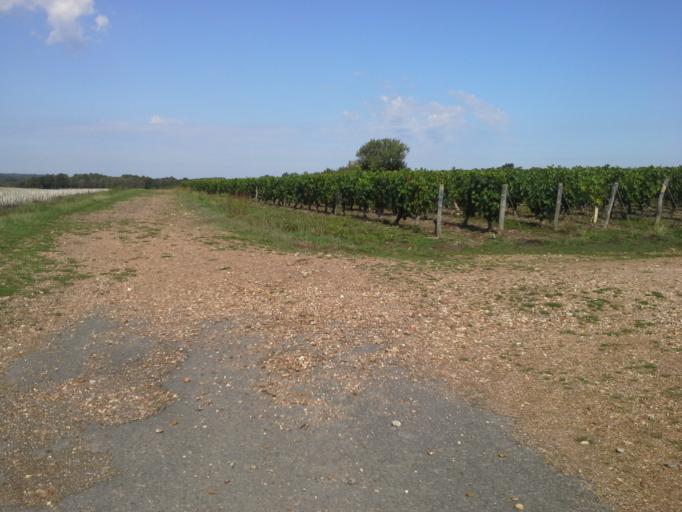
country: FR
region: Centre
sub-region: Departement du Loir-et-Cher
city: Villiers-sur-Loir
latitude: 47.8134
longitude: 0.9792
